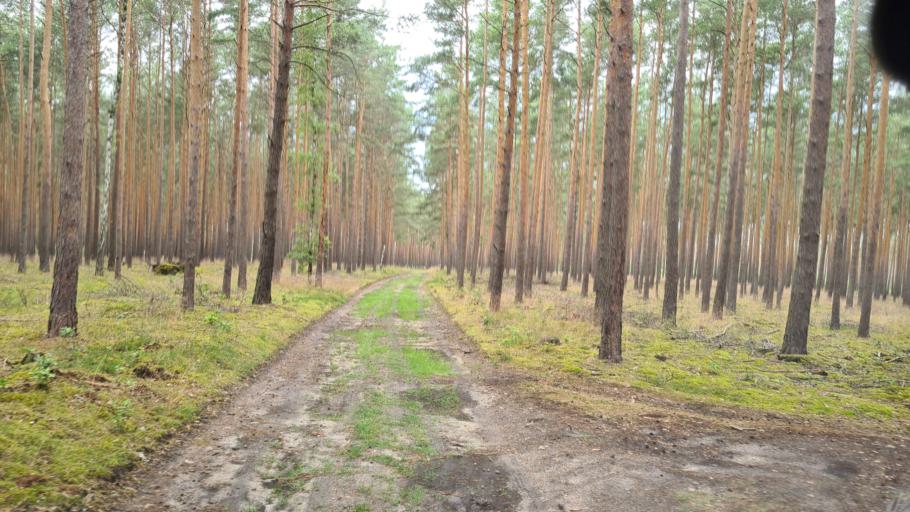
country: DE
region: Brandenburg
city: Bronkow
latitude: 51.7150
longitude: 13.8488
